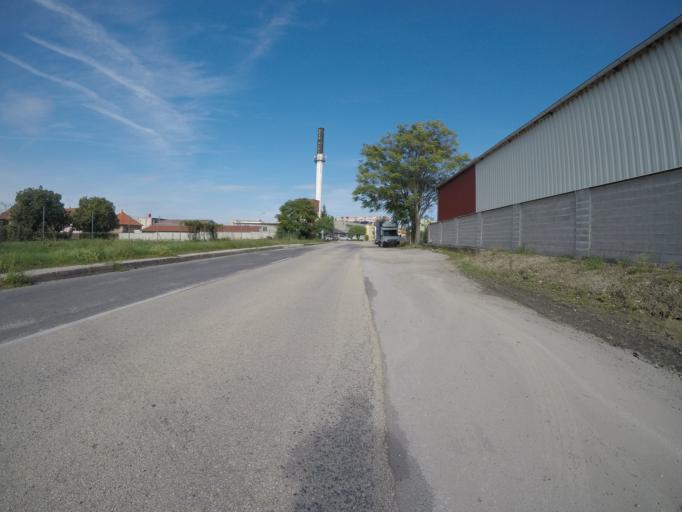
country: SK
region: Trnavsky
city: Dunajska Streda
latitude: 47.9884
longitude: 17.6265
